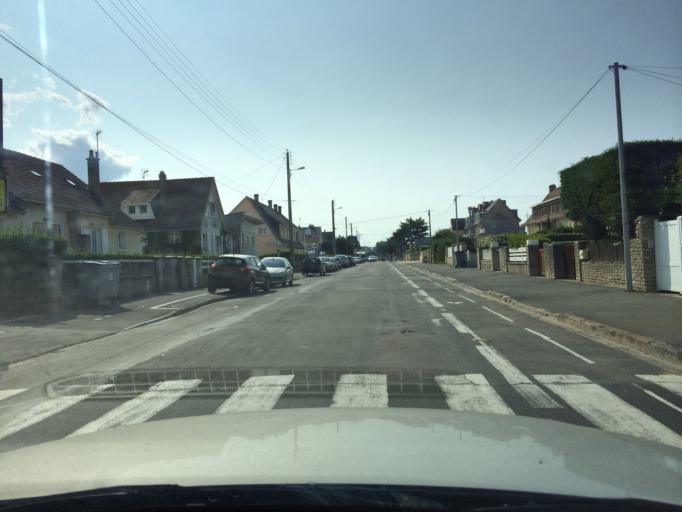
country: FR
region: Lower Normandy
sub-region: Departement du Calvados
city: Courseulles-sur-Mer
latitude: 49.3353
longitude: -0.4536
